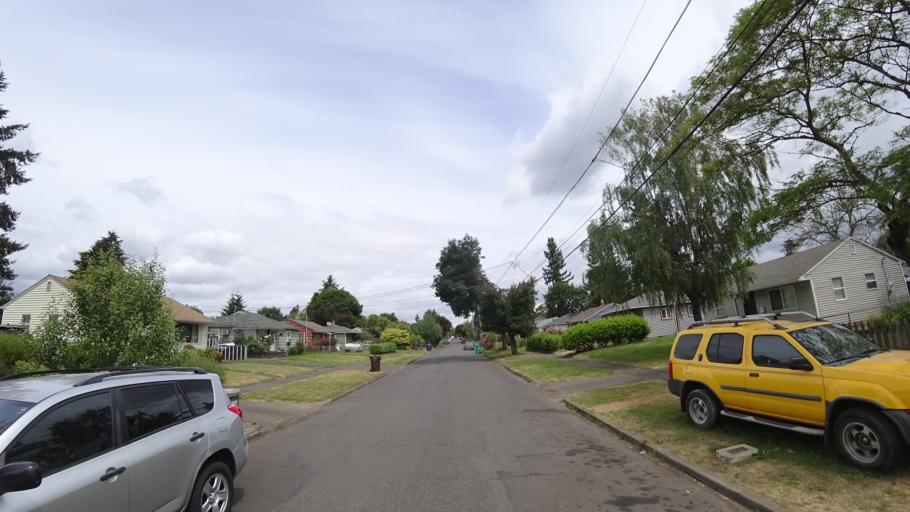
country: US
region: Oregon
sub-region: Multnomah County
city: Lents
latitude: 45.4692
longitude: -122.5748
